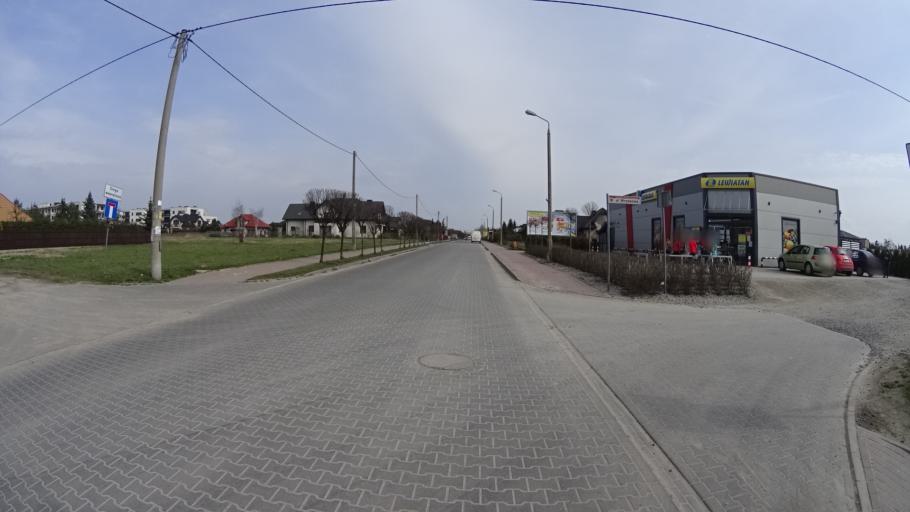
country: PL
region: Masovian Voivodeship
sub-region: Powiat warszawski zachodni
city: Ozarow Mazowiecki
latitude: 52.2138
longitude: 20.7897
